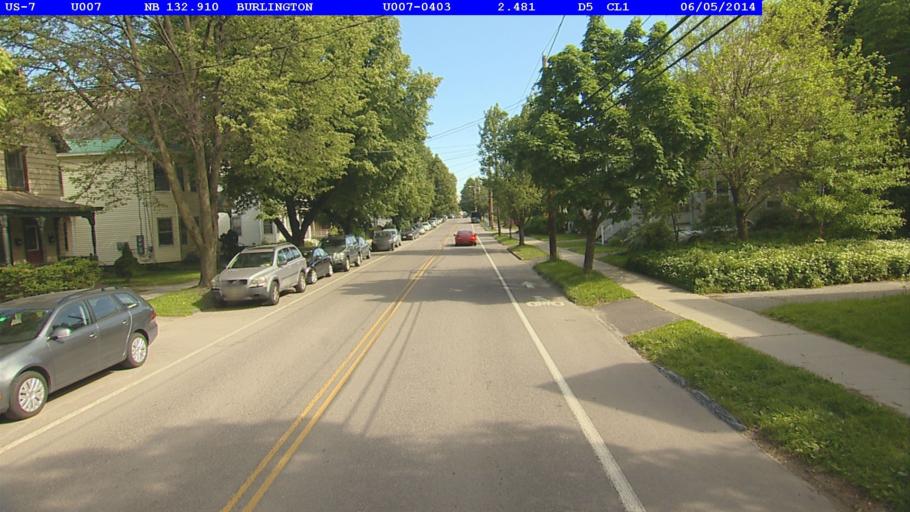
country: US
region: Vermont
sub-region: Chittenden County
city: Burlington
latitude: 44.4814
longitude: -73.2057
